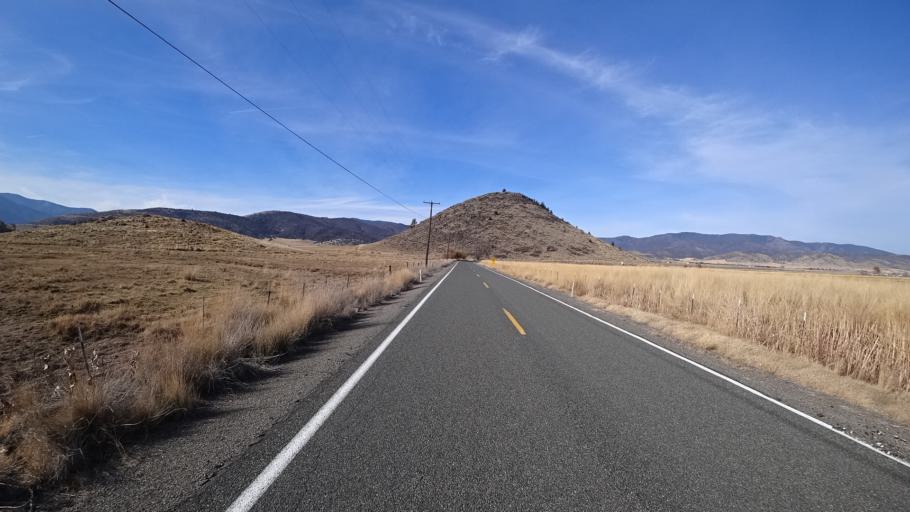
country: US
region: California
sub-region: Siskiyou County
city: Weed
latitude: 41.5342
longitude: -122.5160
